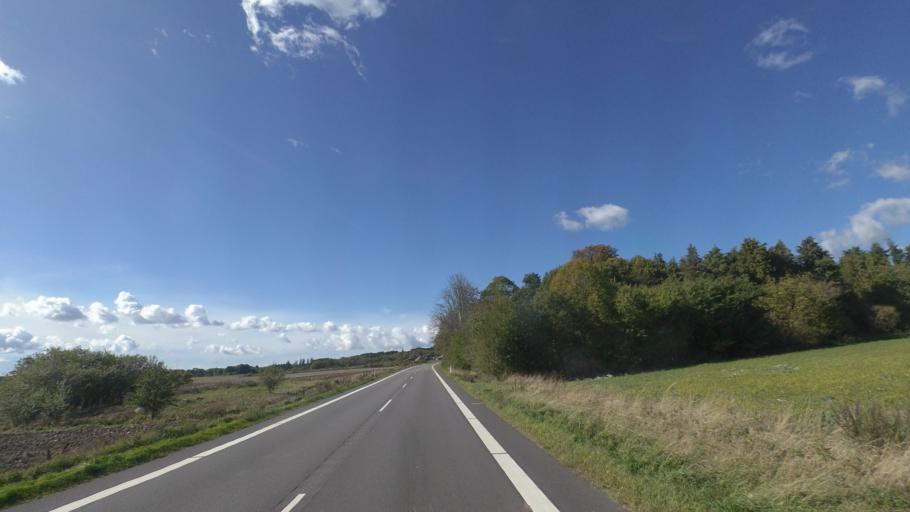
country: DK
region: Capital Region
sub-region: Bornholm Kommune
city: Nexo
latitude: 55.0624
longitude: 15.0319
